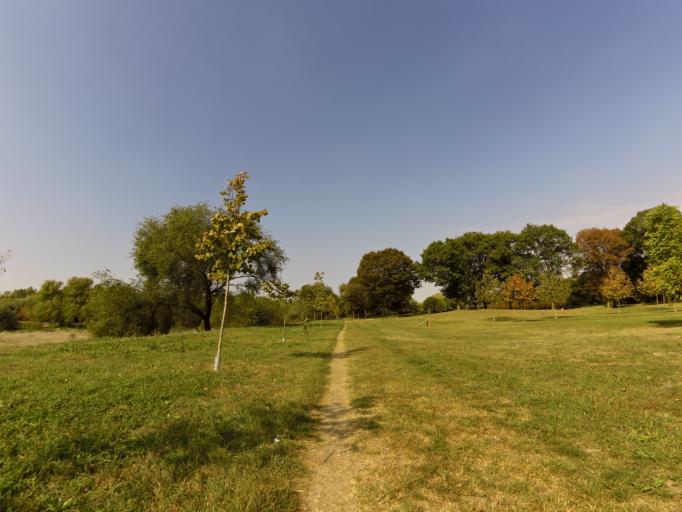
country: IT
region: Lombardy
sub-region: Citta metropolitana di Milano
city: Chiaravalle
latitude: 45.4315
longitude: 9.2343
